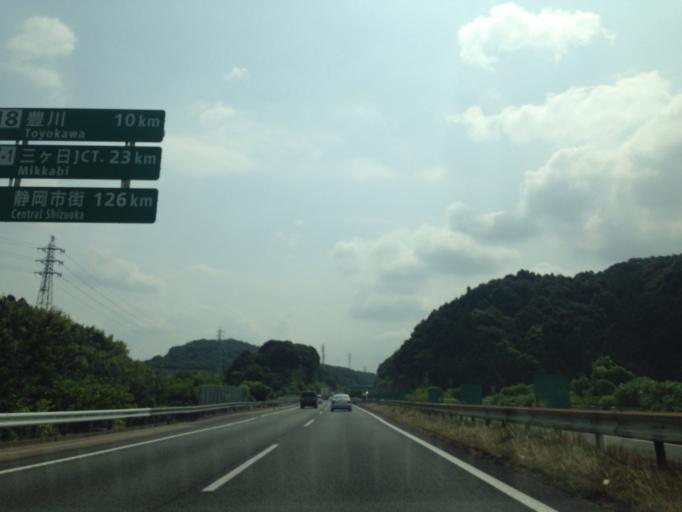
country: JP
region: Aichi
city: Kozakai-cho
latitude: 34.8624
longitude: 137.3155
